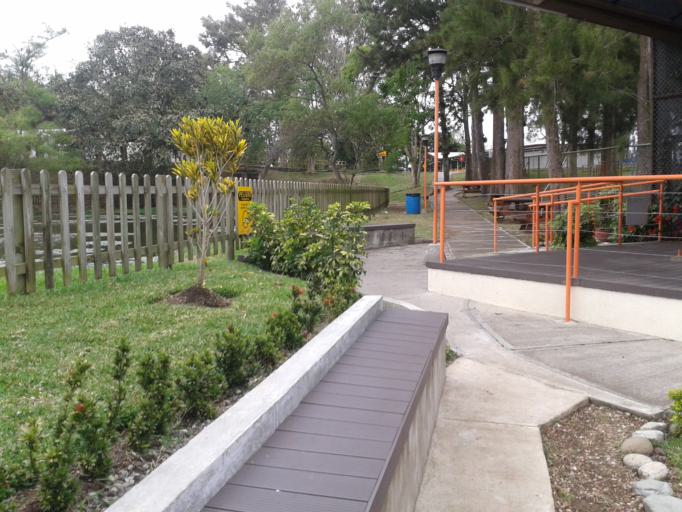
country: CR
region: Cartago
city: Cartago
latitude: 9.8554
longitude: -83.9109
